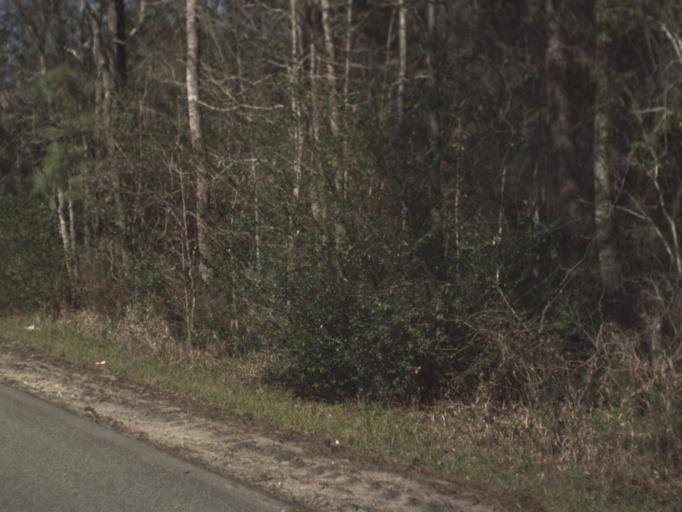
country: US
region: Florida
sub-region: Calhoun County
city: Blountstown
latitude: 30.4579
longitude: -85.0636
